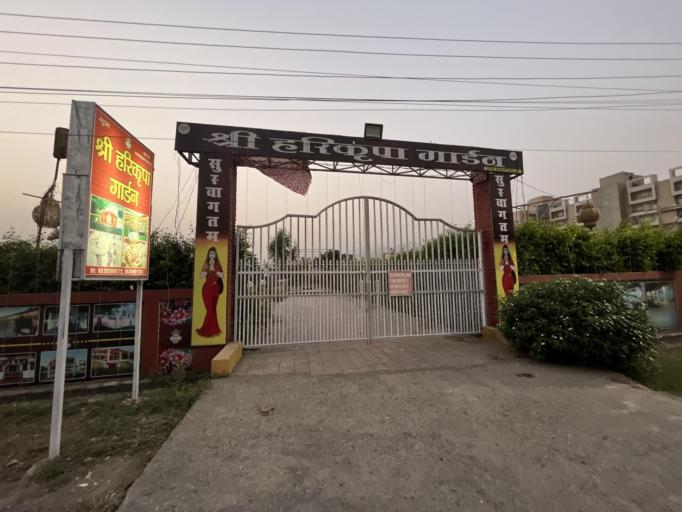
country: IN
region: Uttarakhand
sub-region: Naini Tal
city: Haldwani
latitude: 29.2186
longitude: 79.4907
